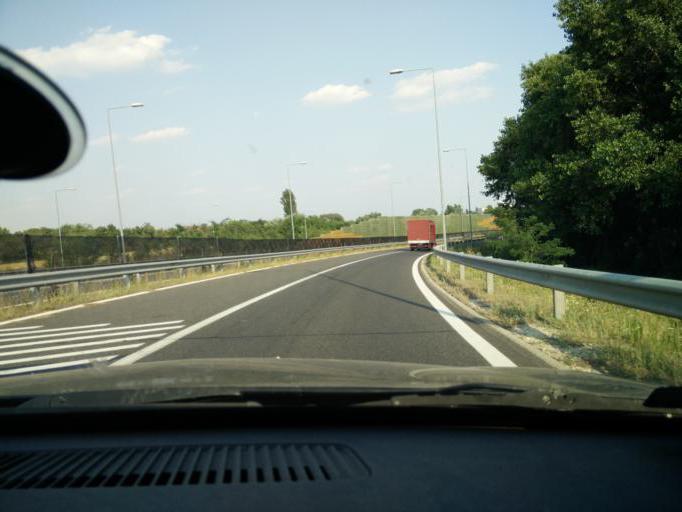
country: HU
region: Pest
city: Diosd
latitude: 47.4012
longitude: 18.9792
